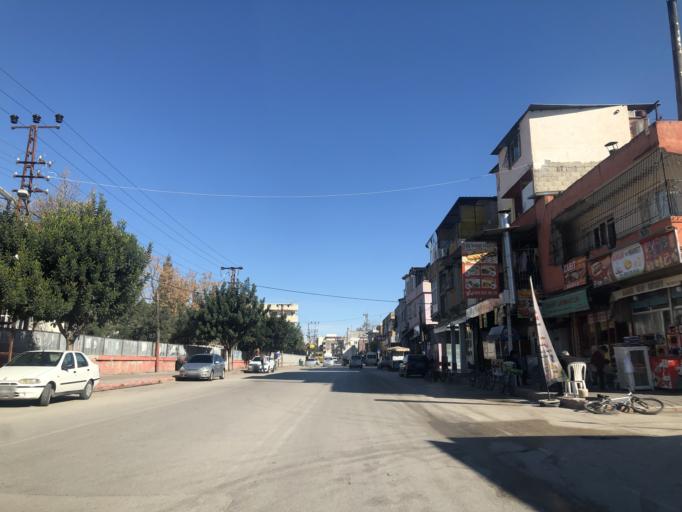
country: TR
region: Adana
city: Yuregir
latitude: 37.0099
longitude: 35.3664
